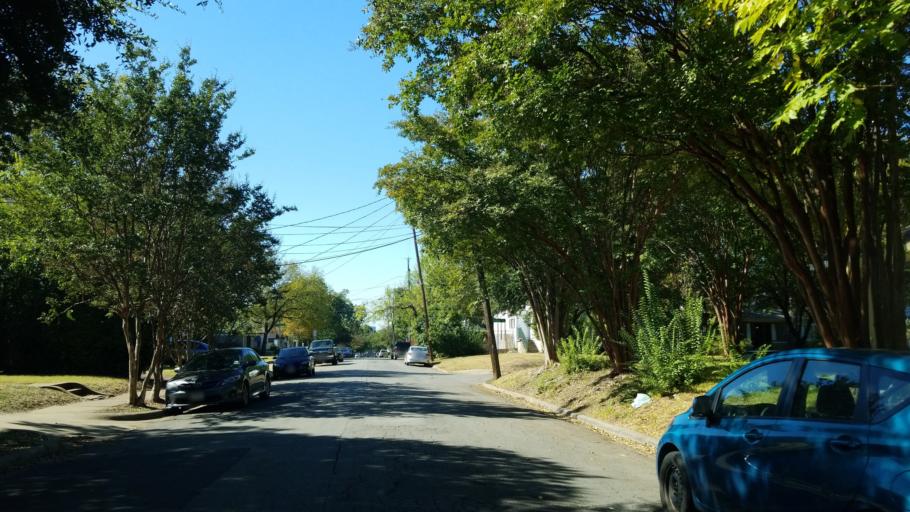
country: US
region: Texas
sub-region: Dallas County
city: Highland Park
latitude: 32.8066
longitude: -96.7587
